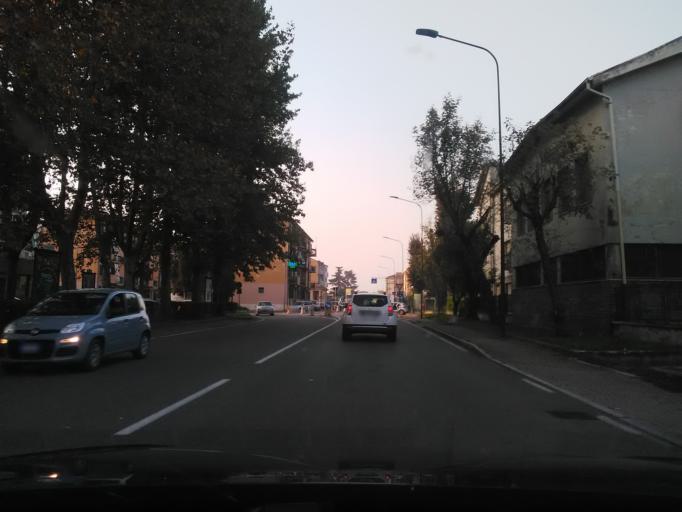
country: IT
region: Piedmont
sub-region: Provincia di Alessandria
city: Casale Monferrato
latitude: 45.1457
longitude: 8.4455
